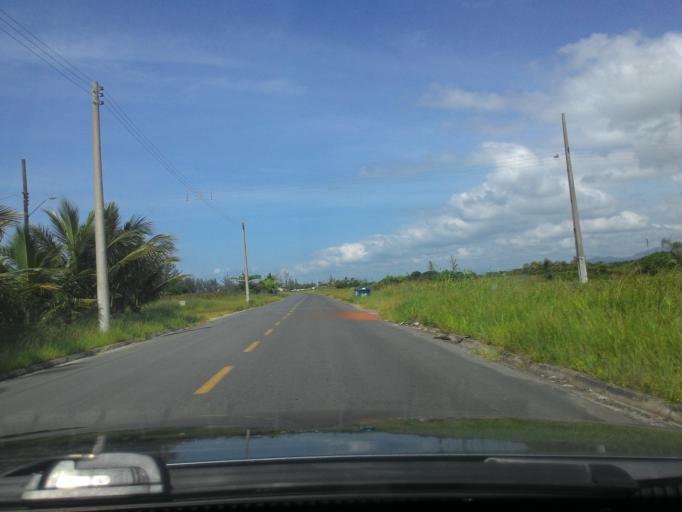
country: BR
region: Sao Paulo
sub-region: Iguape
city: Iguape
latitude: -24.8232
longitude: -47.6613
